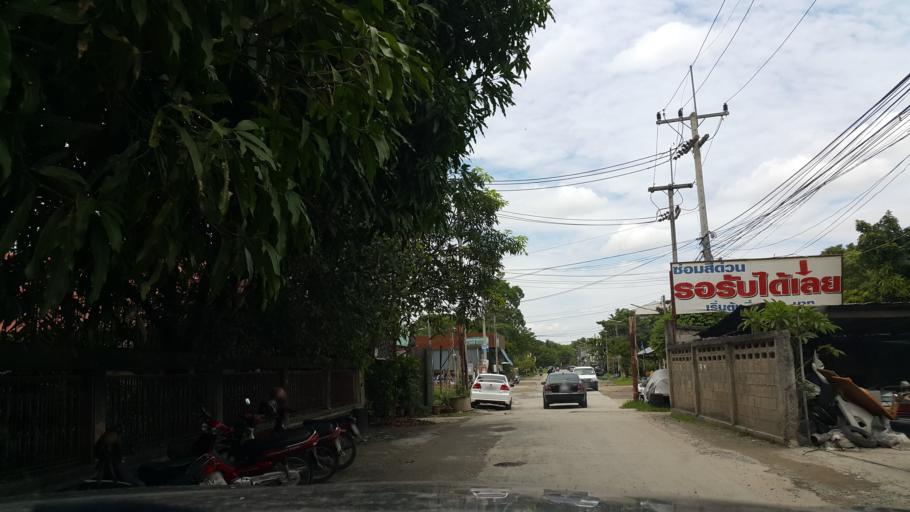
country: TH
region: Chiang Mai
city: Chiang Mai
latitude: 18.8035
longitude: 98.9971
